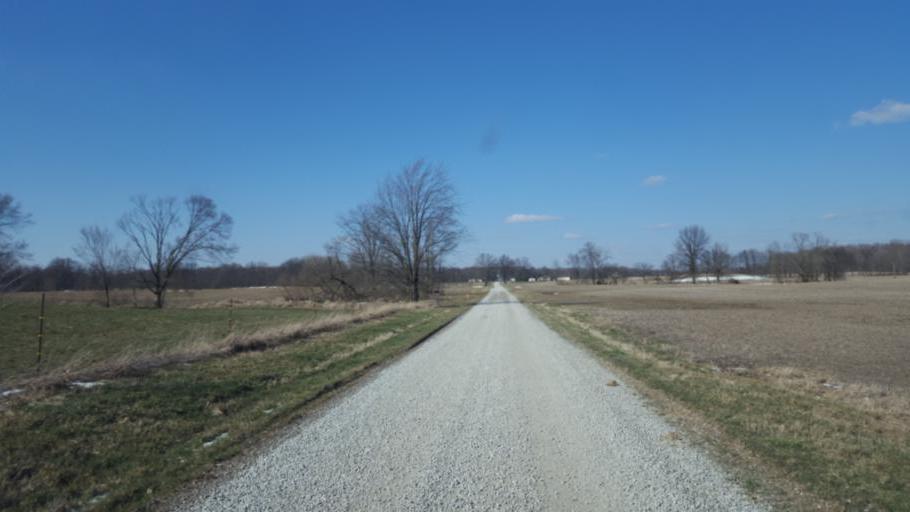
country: US
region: Ohio
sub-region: Morrow County
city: Mount Gilead
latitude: 40.5163
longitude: -82.7782
